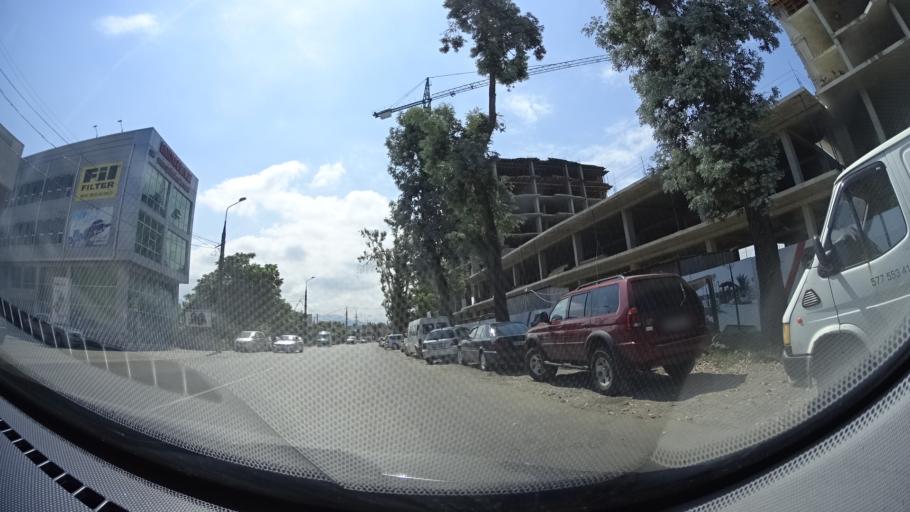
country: GE
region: Ajaria
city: Batumi
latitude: 41.6227
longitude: 41.6146
